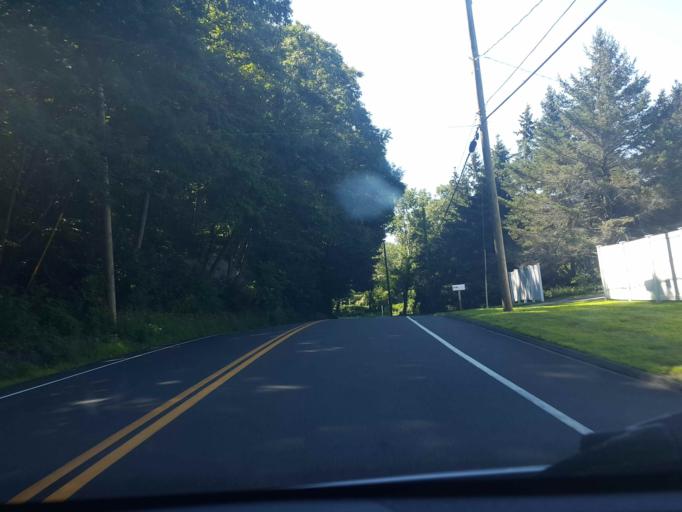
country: US
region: Connecticut
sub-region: New Haven County
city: Guilford
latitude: 41.3338
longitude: -72.7078
